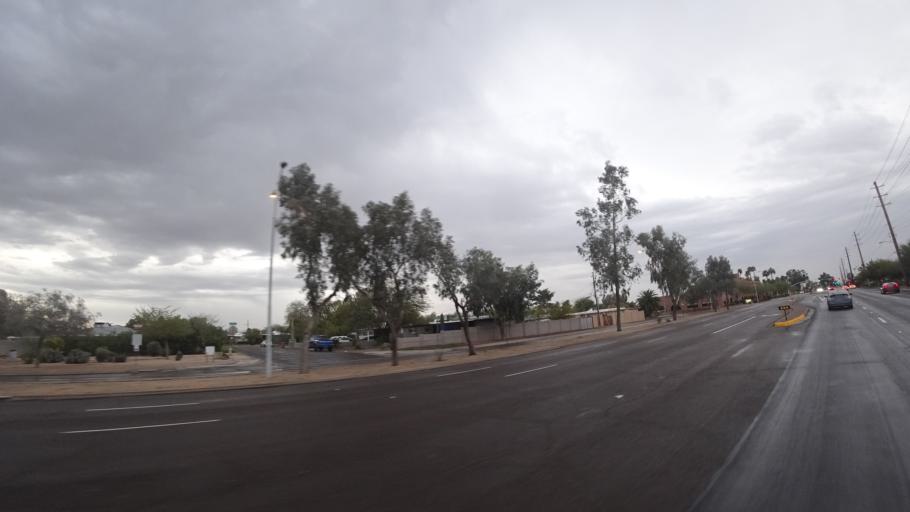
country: US
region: Arizona
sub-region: Maricopa County
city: Scottsdale
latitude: 33.4684
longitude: -111.9089
